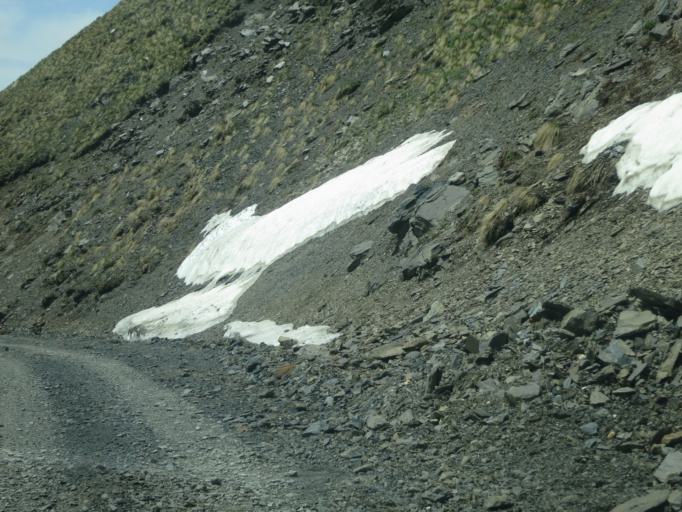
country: GE
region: Kakheti
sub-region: Telavi
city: Telavi
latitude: 42.2761
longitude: 45.4997
